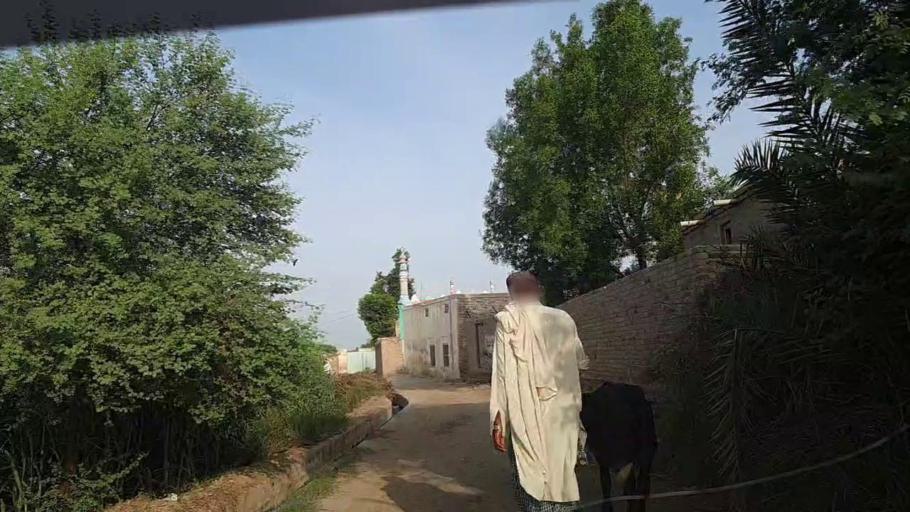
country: PK
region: Sindh
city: Ghotki
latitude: 27.9815
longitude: 69.2539
